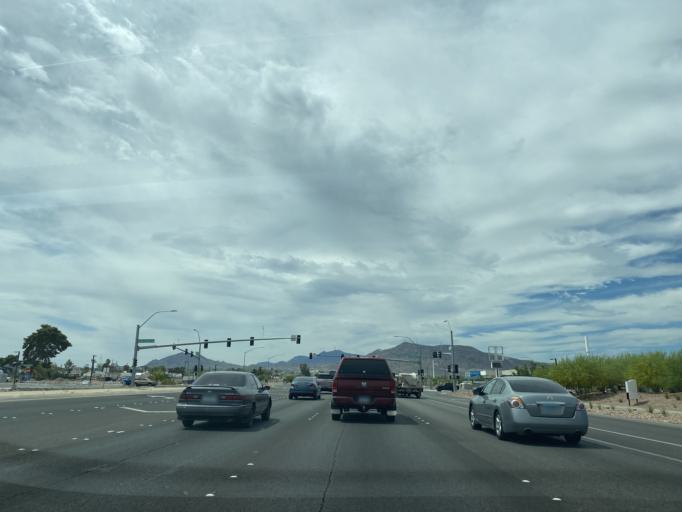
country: US
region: Nevada
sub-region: Clark County
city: Henderson
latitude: 36.0517
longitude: -114.9708
